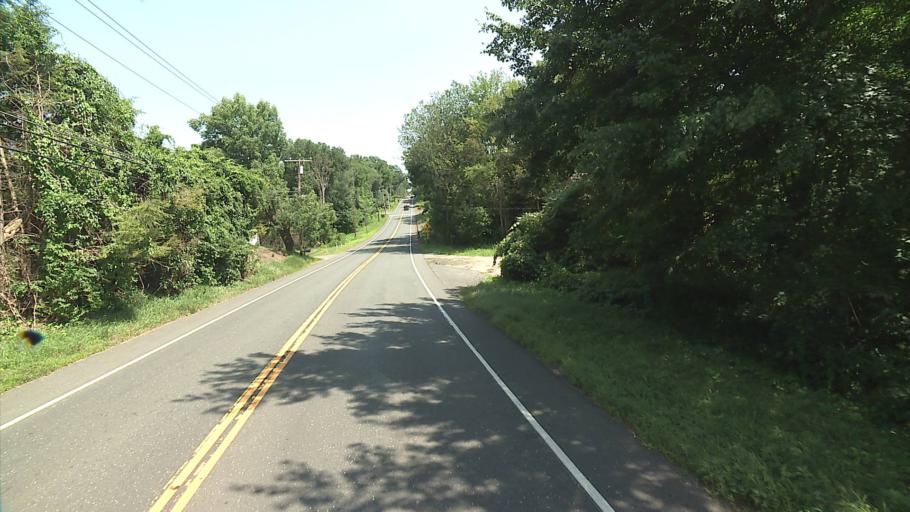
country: US
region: Connecticut
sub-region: Hartford County
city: Salmon Brook
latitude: 41.9524
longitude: -72.7606
